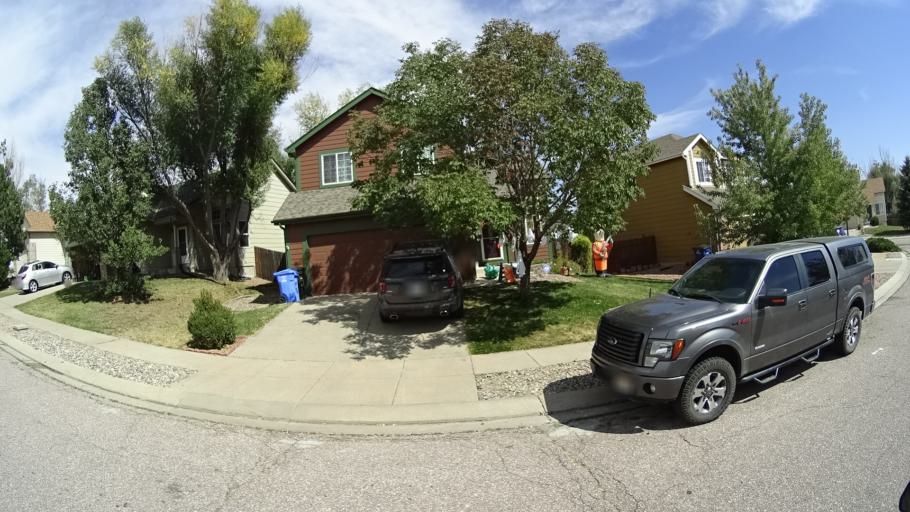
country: US
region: Colorado
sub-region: El Paso County
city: Cimarron Hills
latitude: 38.9011
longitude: -104.7133
